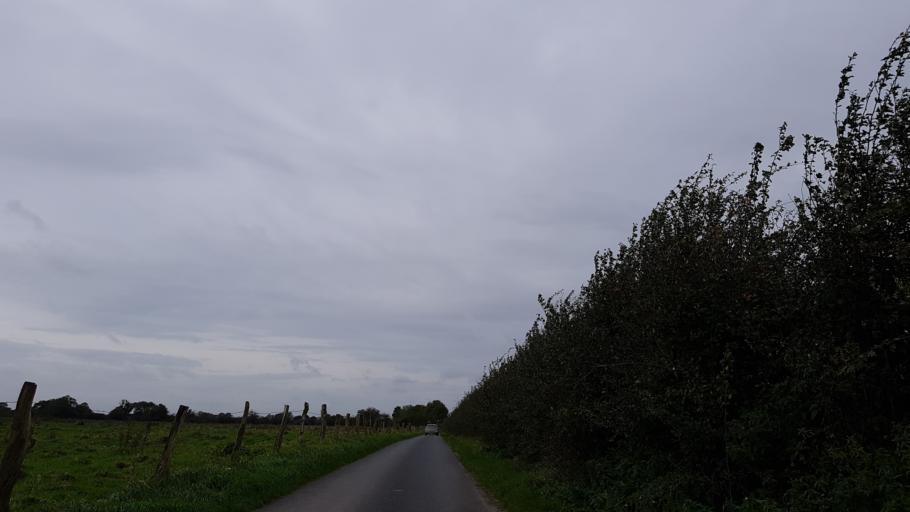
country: DE
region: Lower Saxony
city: Ahsen-Oetzen
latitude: 52.9911
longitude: 9.0705
